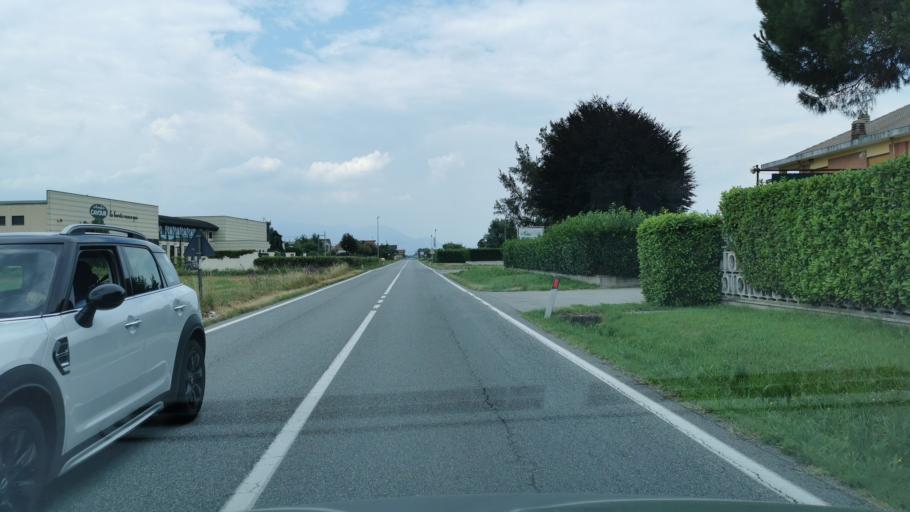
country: IT
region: Piedmont
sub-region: Provincia di Torino
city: Cavour
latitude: 44.8009
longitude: 7.3737
